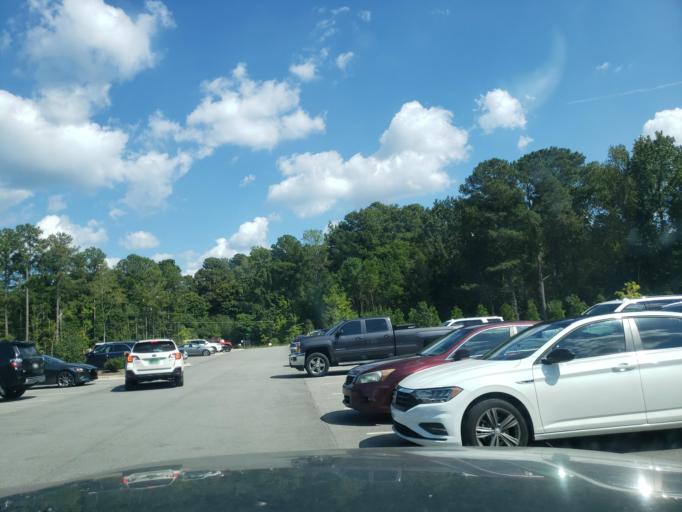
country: US
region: North Carolina
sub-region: Wake County
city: West Raleigh
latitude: 35.9379
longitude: -78.6963
